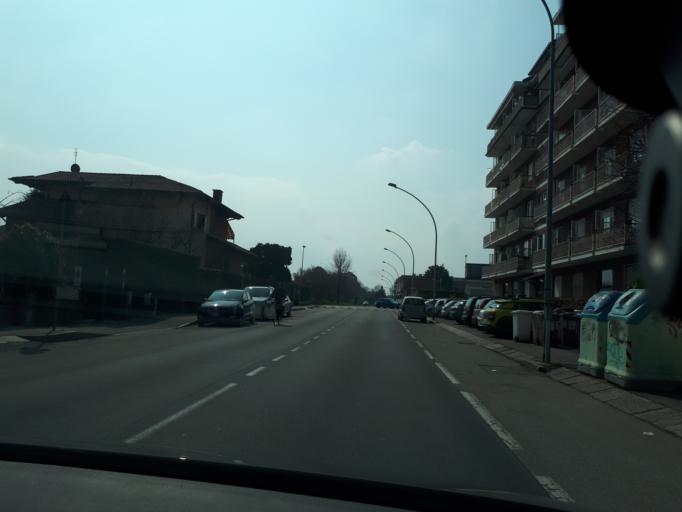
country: IT
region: Piedmont
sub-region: Provincia di Torino
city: Lesna
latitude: 45.0627
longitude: 7.6069
